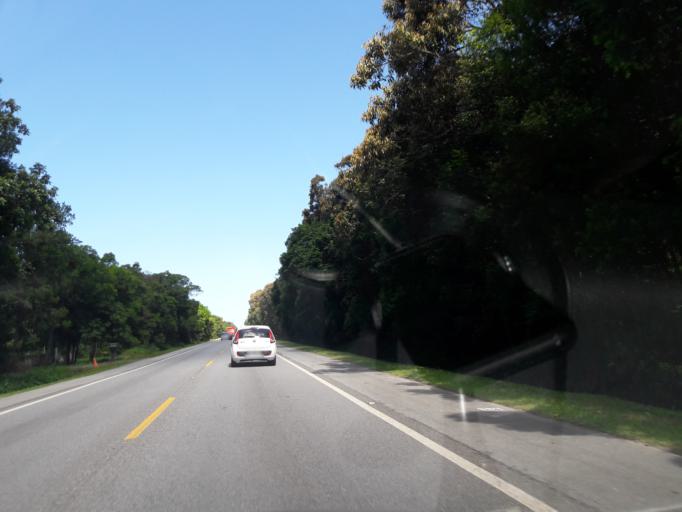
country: BR
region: Parana
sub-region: Pontal Do Parana
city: Pontal do Parana
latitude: -25.6214
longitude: -48.5451
